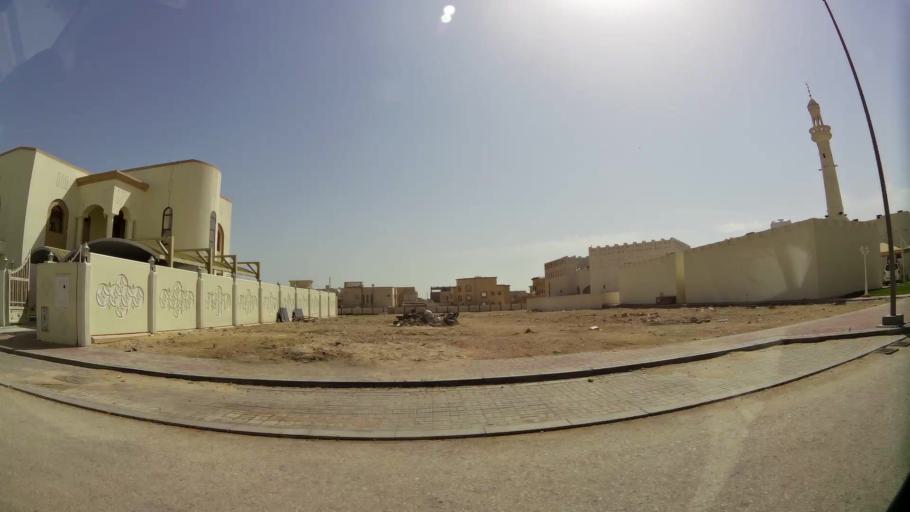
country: QA
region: Baladiyat ad Dawhah
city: Doha
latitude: 25.3612
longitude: 51.4960
